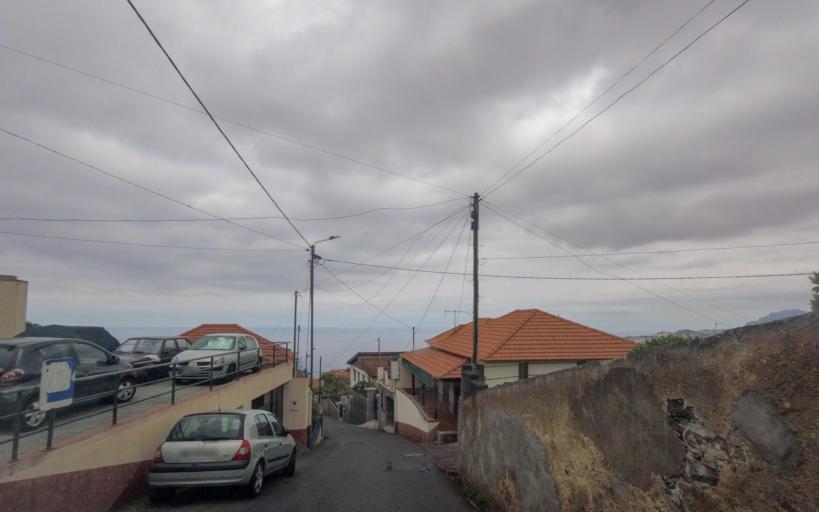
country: PT
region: Madeira
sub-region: Funchal
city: Nossa Senhora do Monte
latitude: 32.6597
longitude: -16.8798
